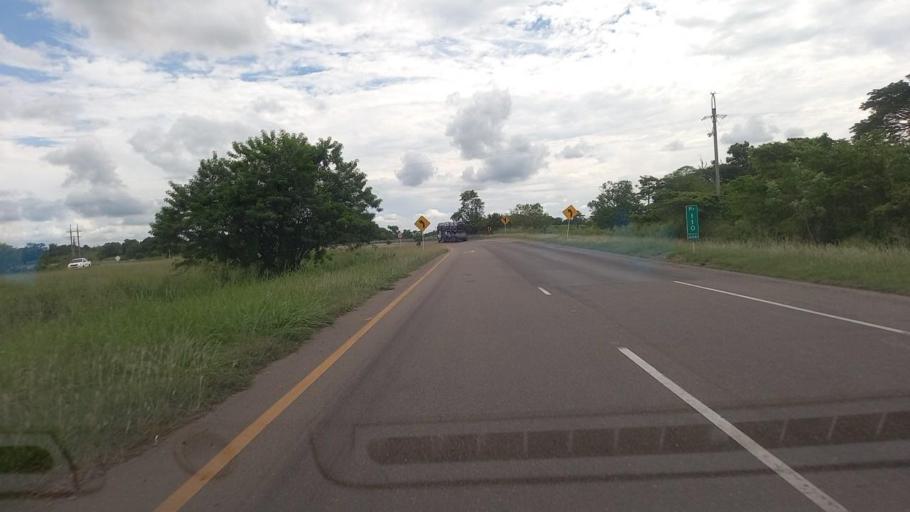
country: CO
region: Boyaca
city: Puerto Boyaca
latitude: 6.0559
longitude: -74.5615
